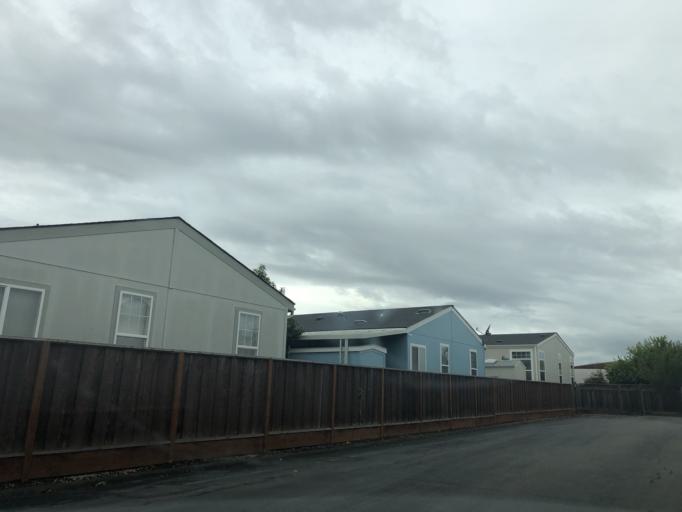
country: US
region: California
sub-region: Santa Clara County
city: Sunnyvale
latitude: 37.4006
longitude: -122.0020
